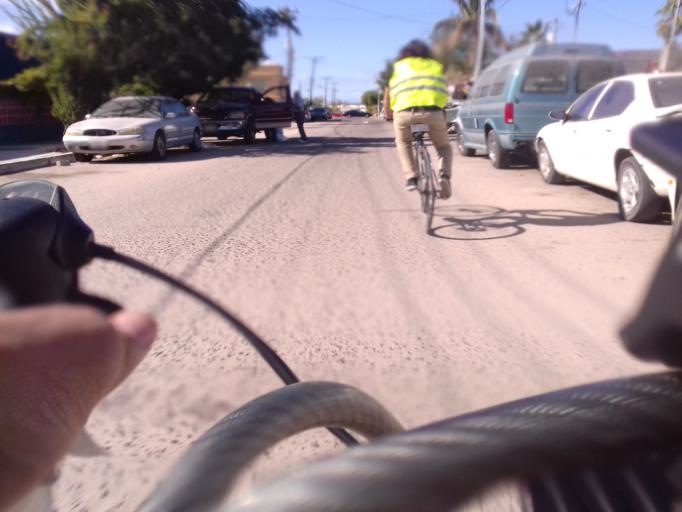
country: MX
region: Baja California Sur
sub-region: La Paz
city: La Paz
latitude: 24.1503
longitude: -110.3287
